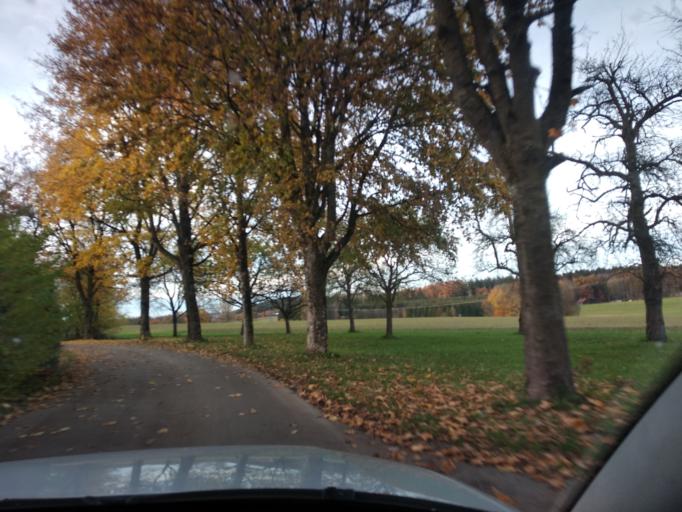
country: DE
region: Bavaria
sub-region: Upper Bavaria
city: Grafing bei Munchen
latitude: 48.0350
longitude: 11.9892
